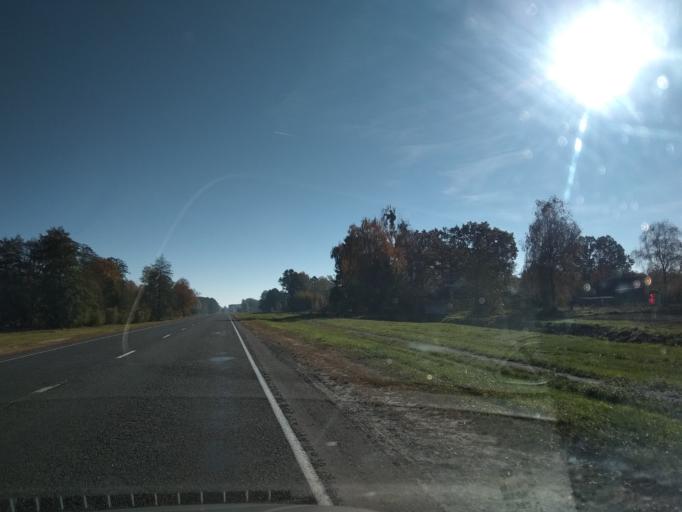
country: BY
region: Brest
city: Malaryta
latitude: 51.8318
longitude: 24.2740
